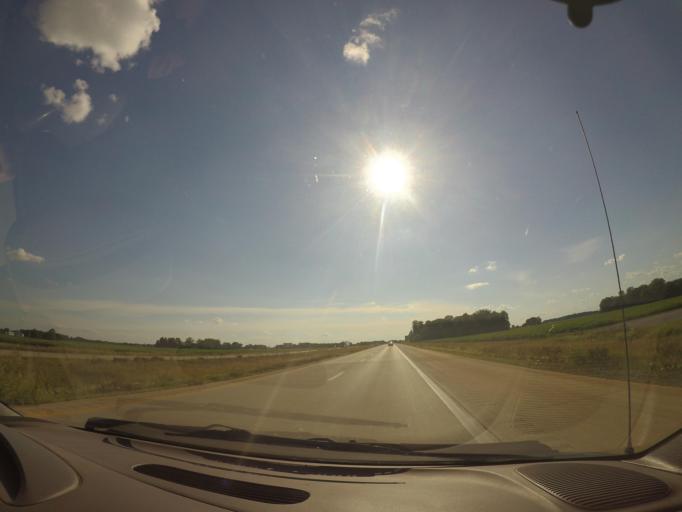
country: US
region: Ohio
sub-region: Lucas County
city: Whitehouse
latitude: 41.4561
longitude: -83.8056
